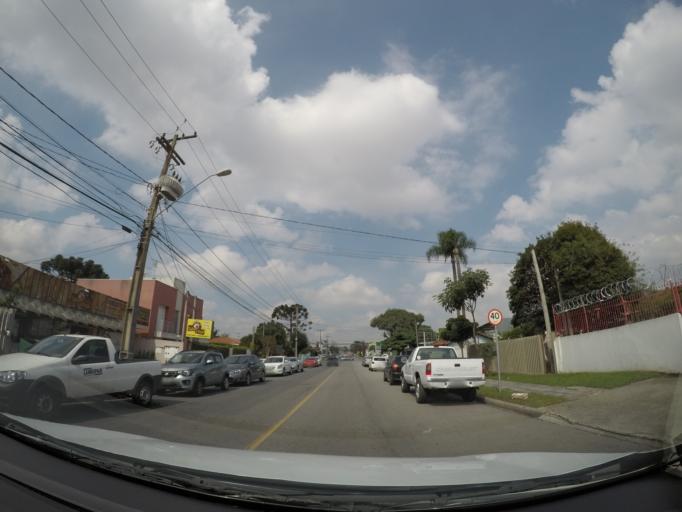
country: BR
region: Parana
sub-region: Sao Jose Dos Pinhais
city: Sao Jose dos Pinhais
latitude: -25.4880
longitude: -49.2510
